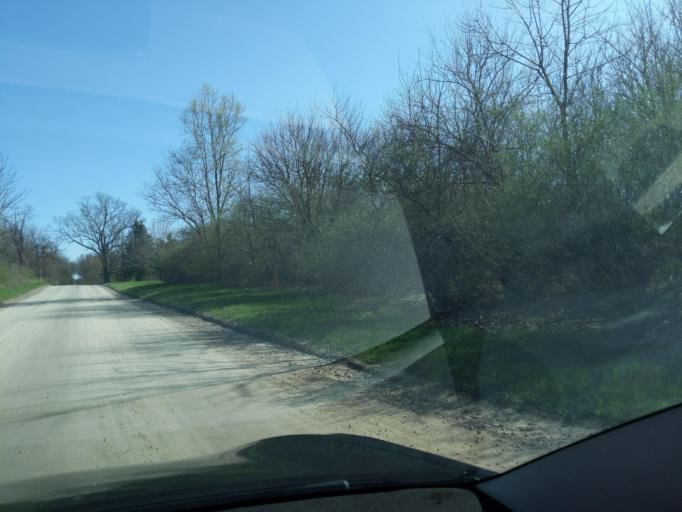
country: US
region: Michigan
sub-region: Ingham County
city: Stockbridge
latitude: 42.4067
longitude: -84.0837
